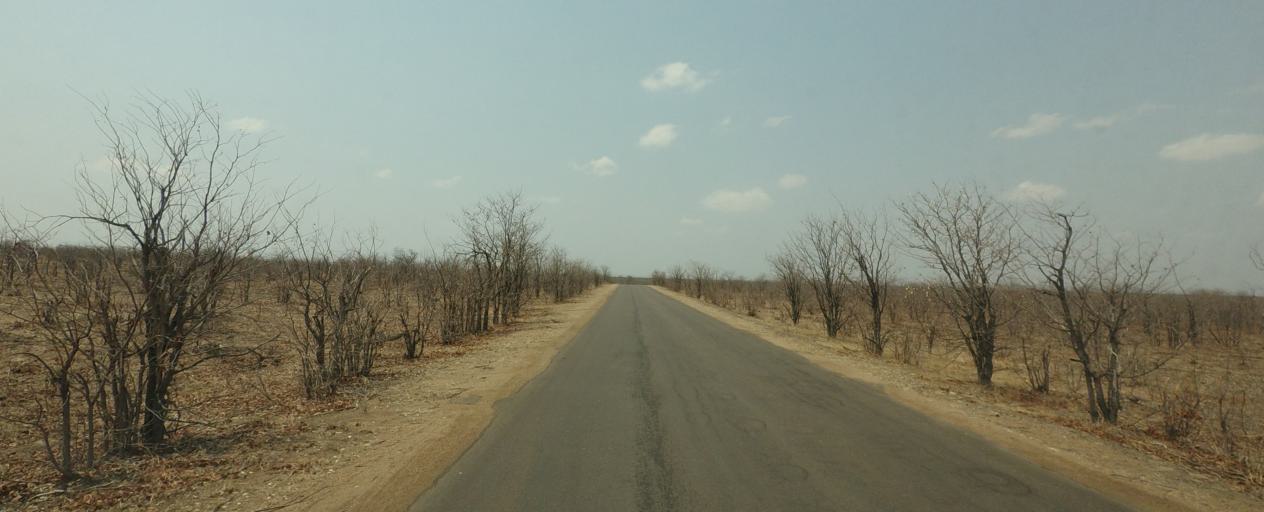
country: ZA
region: Limpopo
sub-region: Mopani District Municipality
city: Phalaborwa
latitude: -23.5178
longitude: 31.4064
